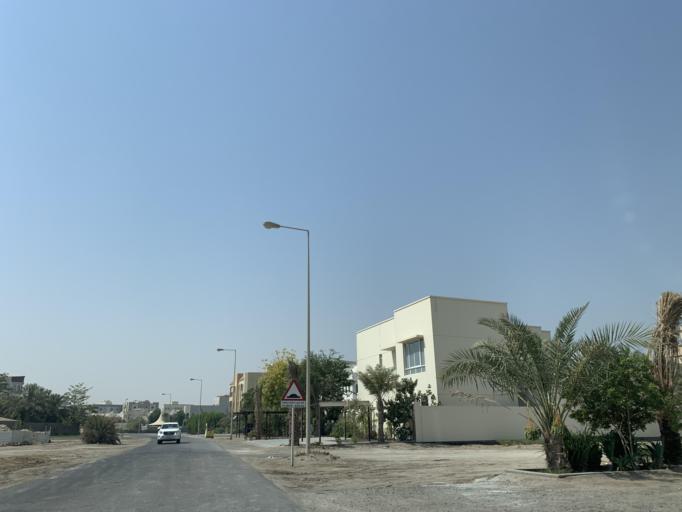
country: BH
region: Manama
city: Jidd Hafs
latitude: 26.1974
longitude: 50.5131
